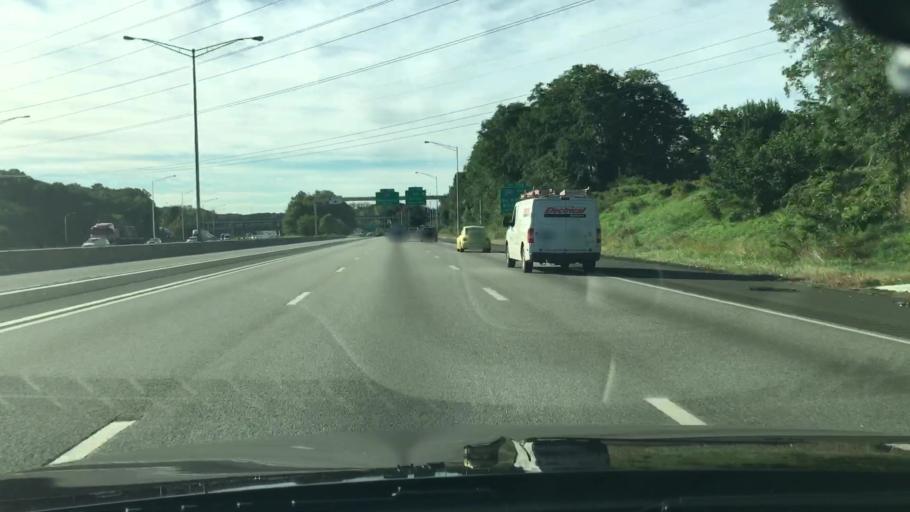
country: US
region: Connecticut
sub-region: Hartford County
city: Blue Hills
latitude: 41.8256
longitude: -72.6660
